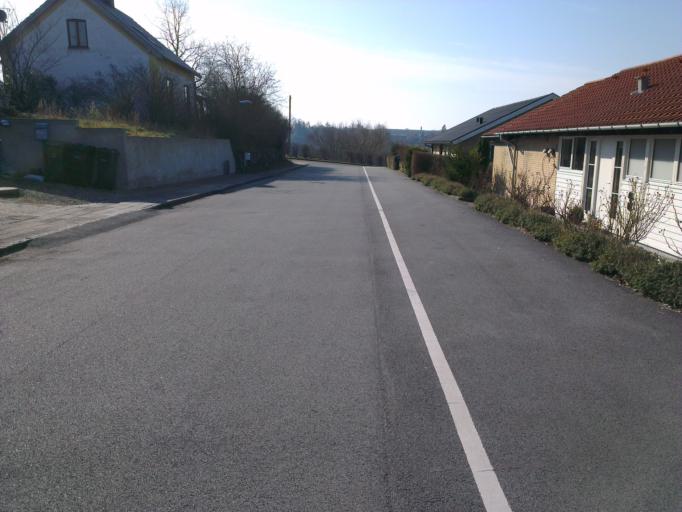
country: DK
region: Capital Region
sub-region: Frederikssund Kommune
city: Frederikssund
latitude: 55.8392
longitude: 12.0766
